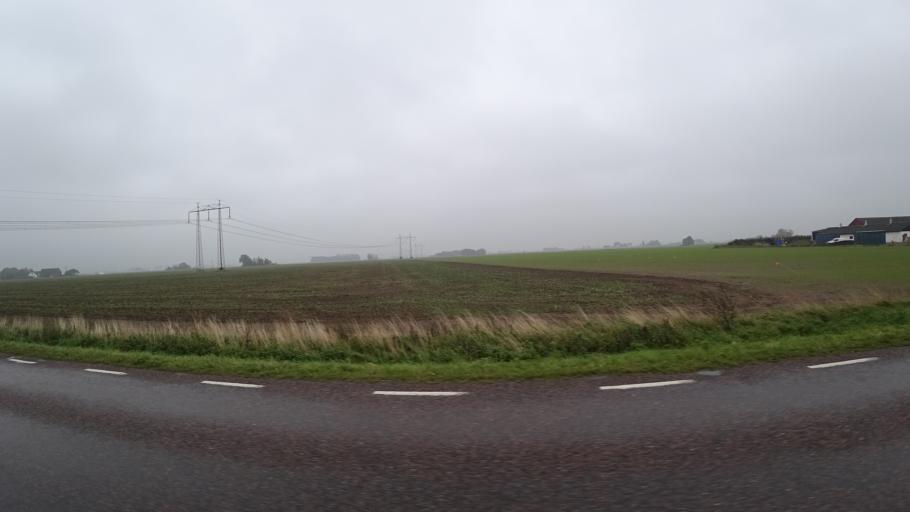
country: SE
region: Skane
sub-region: Kavlinge Kommun
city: Kaevlinge
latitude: 55.8091
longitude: 13.1597
